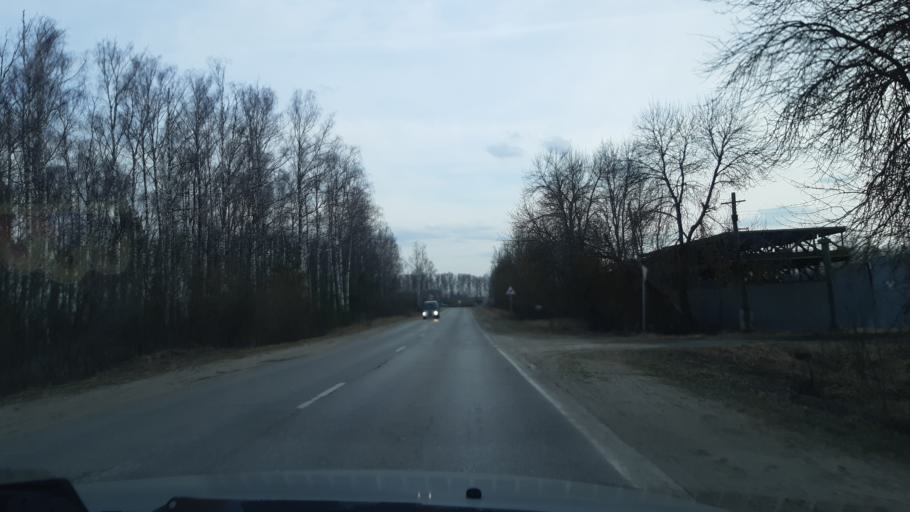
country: RU
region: Vladimir
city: Luknovo
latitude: 56.2263
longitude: 42.0347
